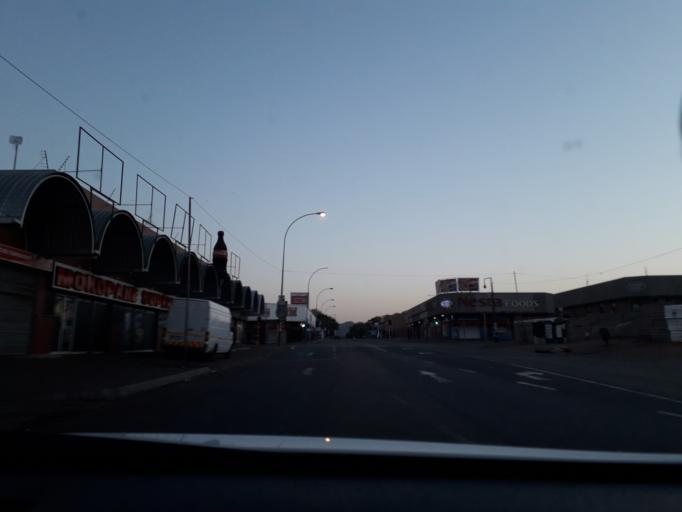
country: ZA
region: Limpopo
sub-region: Waterberg District Municipality
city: Mokopane
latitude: -24.1815
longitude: 29.0136
